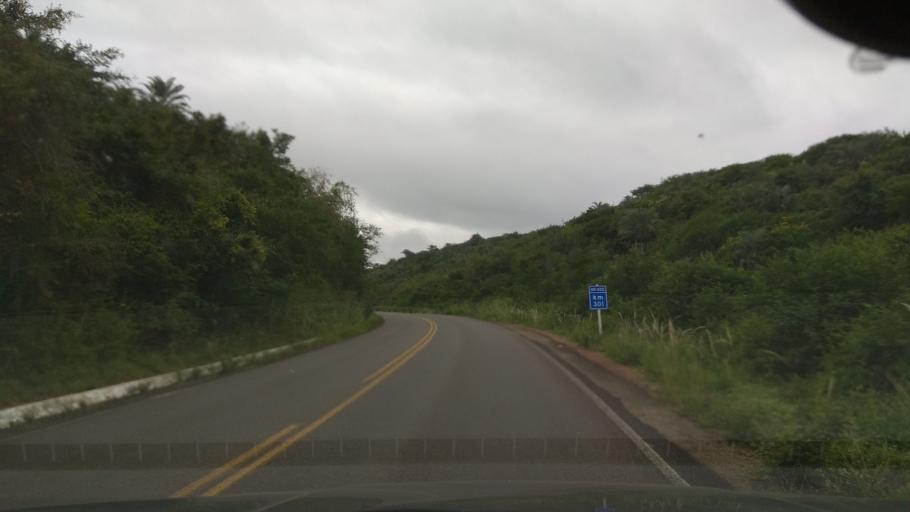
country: BR
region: Bahia
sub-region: Santa Ines
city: Santa Ines
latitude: -13.2589
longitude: -39.7832
